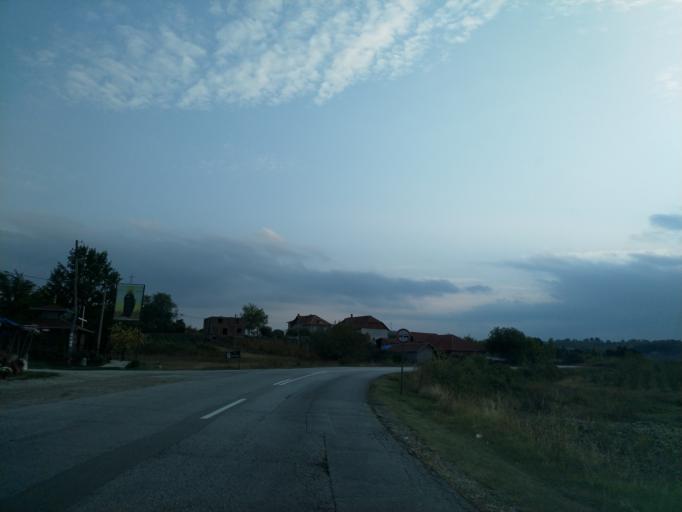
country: RS
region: Central Serbia
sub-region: Sumadijski Okrug
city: Topola
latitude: 44.1891
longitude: 20.7369
